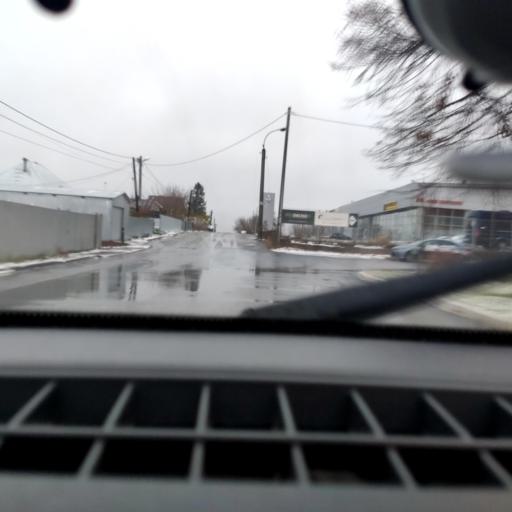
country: RU
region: Bashkortostan
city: Ufa
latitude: 54.7524
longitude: 55.9750
